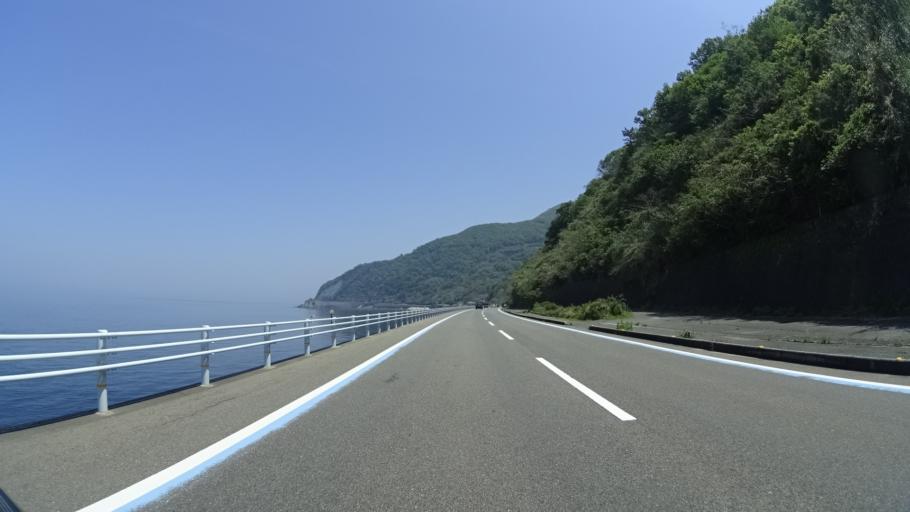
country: JP
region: Ehime
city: Ozu
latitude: 33.5851
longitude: 132.4513
